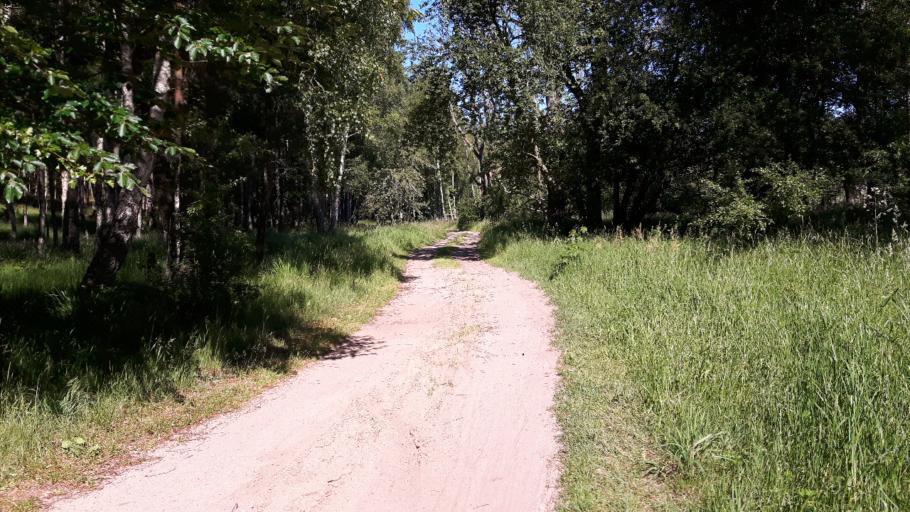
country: PL
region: Pomeranian Voivodeship
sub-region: Powiat leborski
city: Leba
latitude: 54.6978
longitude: 17.4826
